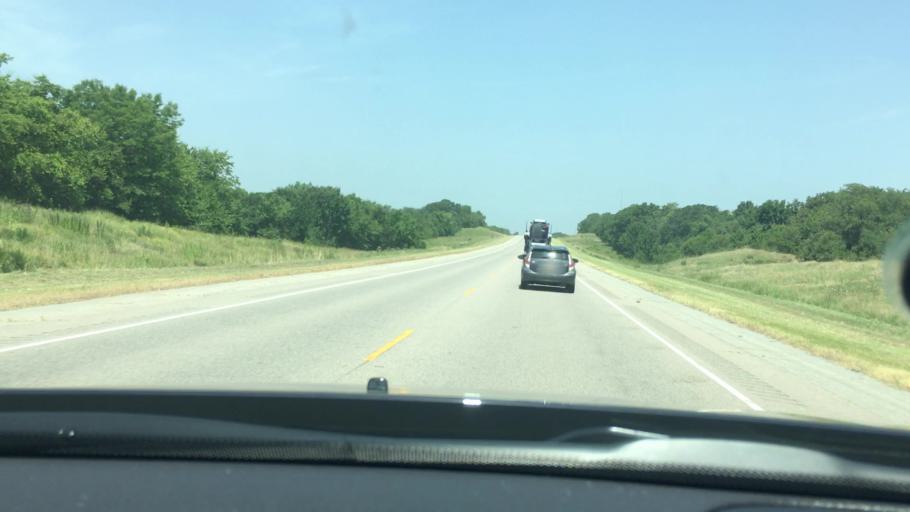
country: US
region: Oklahoma
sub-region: Coal County
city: Coalgate
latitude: 34.6248
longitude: -96.4600
